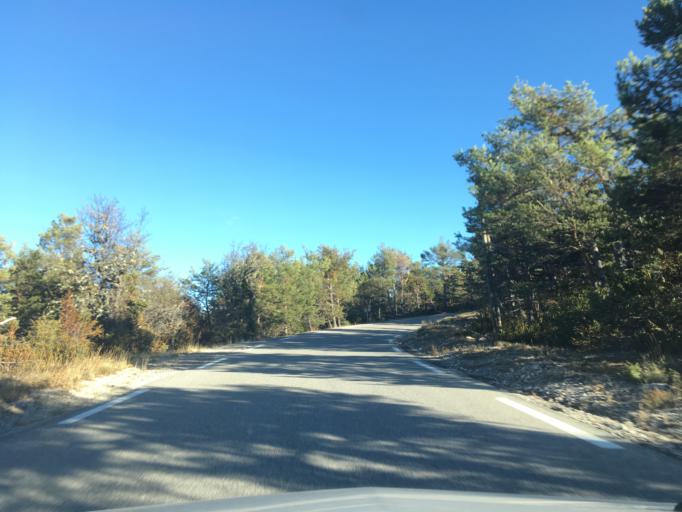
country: FR
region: Provence-Alpes-Cote d'Azur
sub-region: Departement des Alpes-de-Haute-Provence
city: Castellane
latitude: 43.7458
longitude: 6.4350
